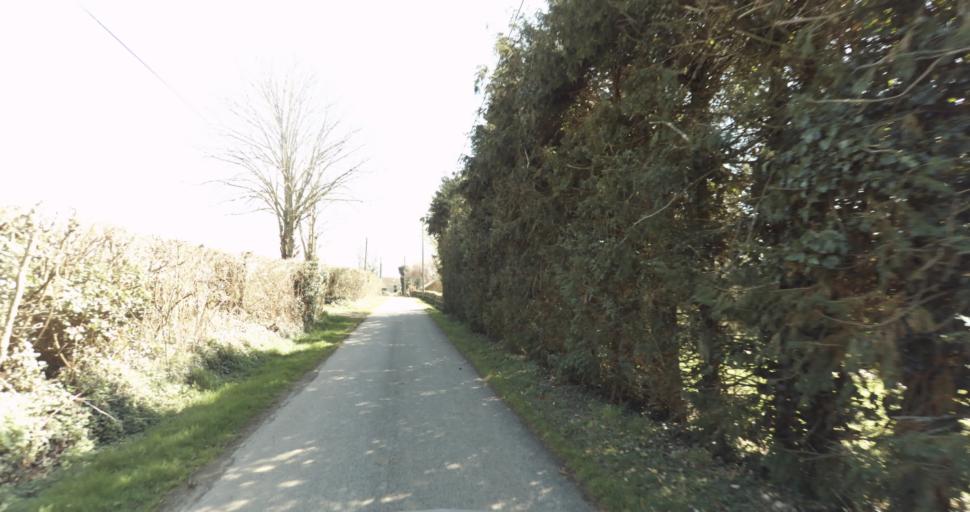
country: FR
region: Lower Normandy
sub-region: Departement du Calvados
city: Saint-Pierre-sur-Dives
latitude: 49.0681
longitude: -0.0343
